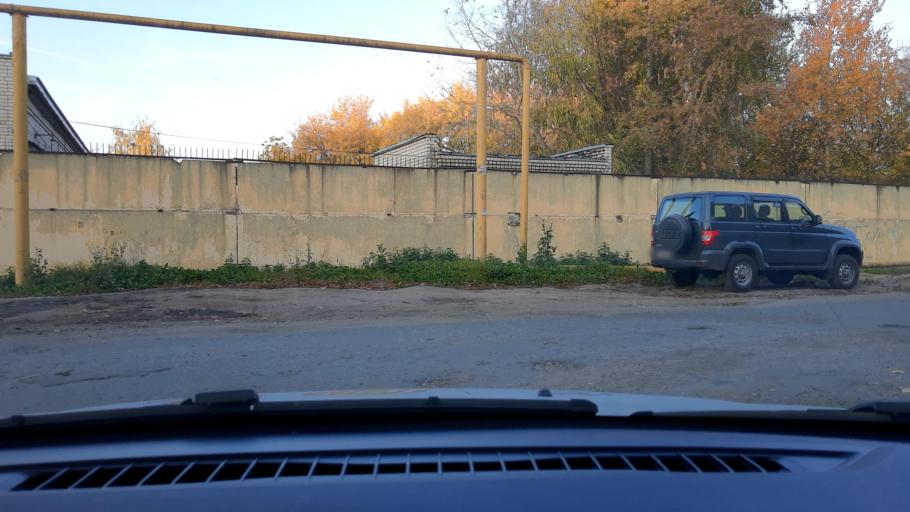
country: RU
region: Nizjnij Novgorod
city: Gorbatovka
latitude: 56.2561
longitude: 43.8781
